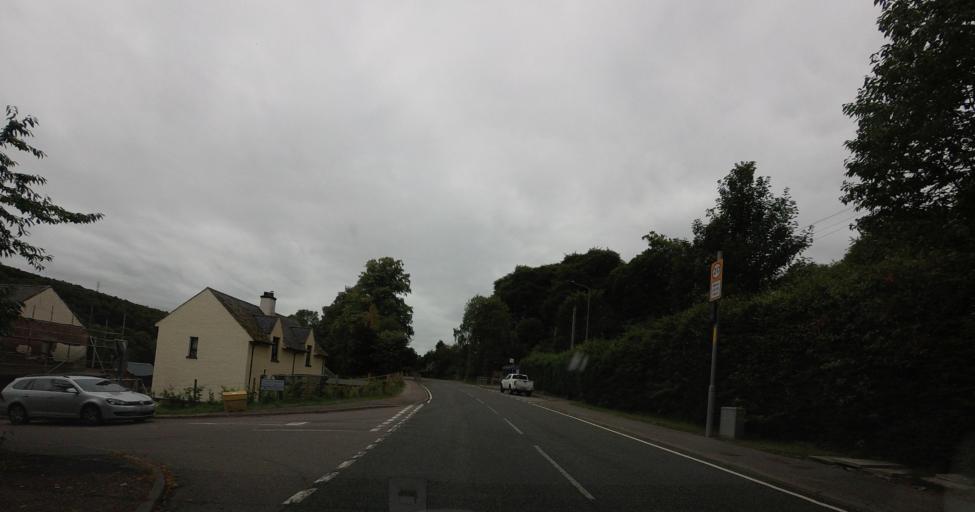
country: GB
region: Scotland
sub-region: Highland
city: Spean Bridge
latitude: 57.0685
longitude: -4.8005
